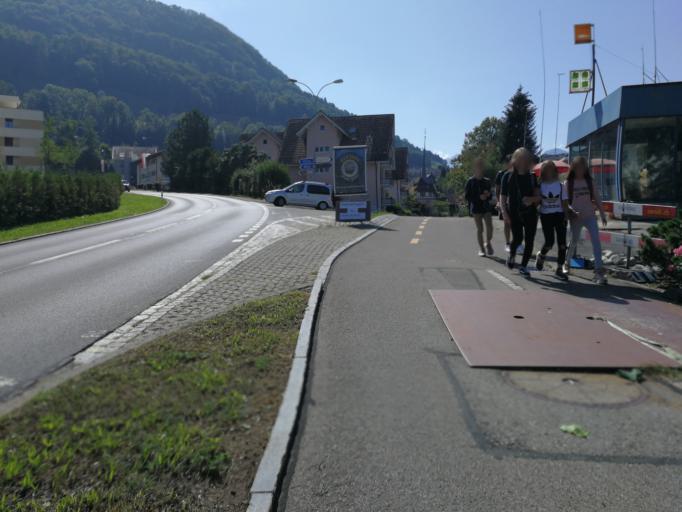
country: CH
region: Lucerne
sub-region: Lucerne-Land District
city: Weggis
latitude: 47.0575
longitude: 8.4293
